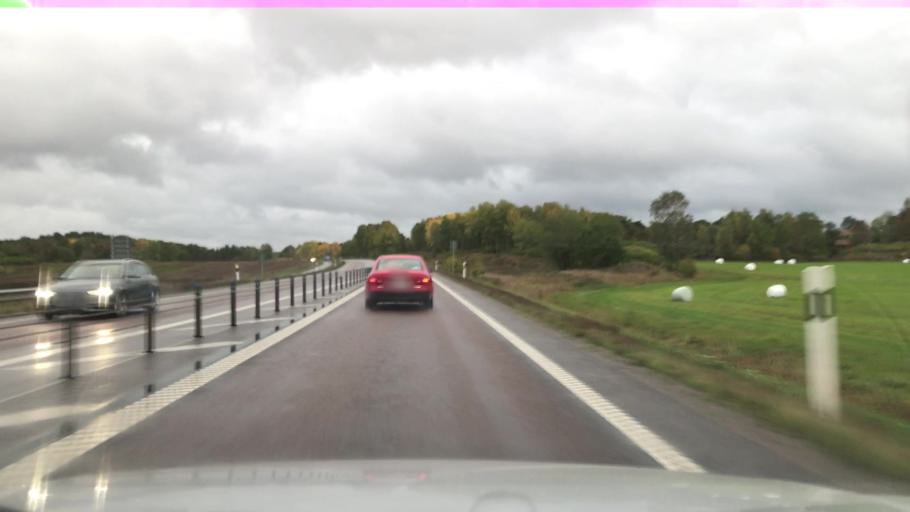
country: SE
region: OEstergoetland
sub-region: Soderkopings Kommun
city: Soederkoeping
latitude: 58.5144
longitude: 16.2887
